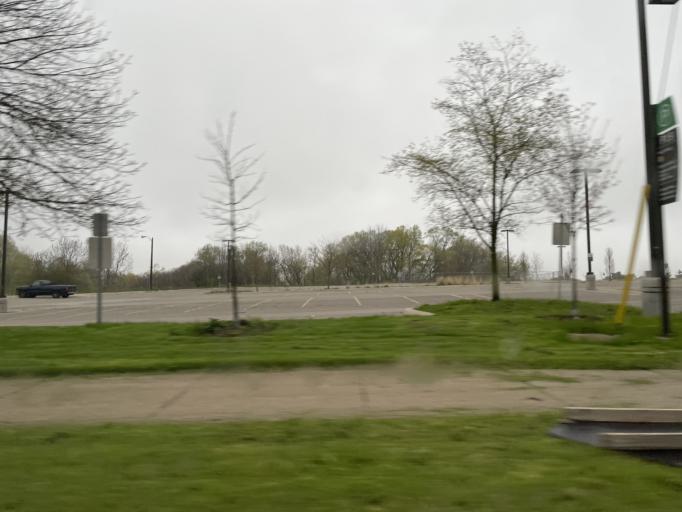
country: CA
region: Ontario
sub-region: Wellington County
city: Guelph
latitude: 43.5356
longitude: -80.2280
